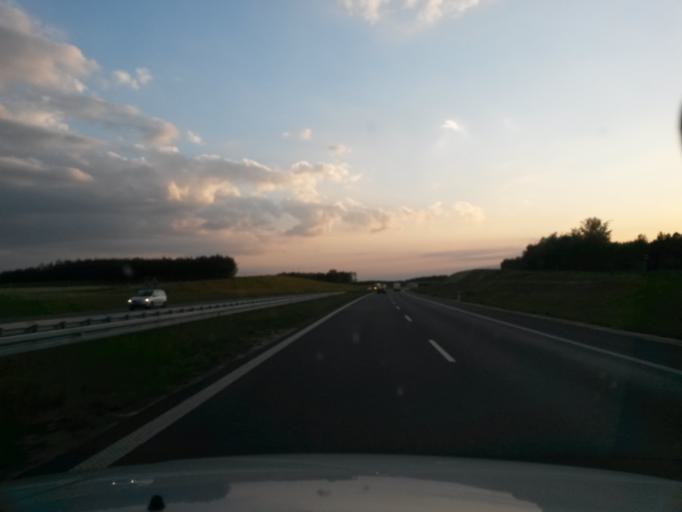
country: PL
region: Lodz Voivodeship
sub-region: Powiat wieruszowski
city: Wieruszow
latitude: 51.3055
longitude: 18.2130
